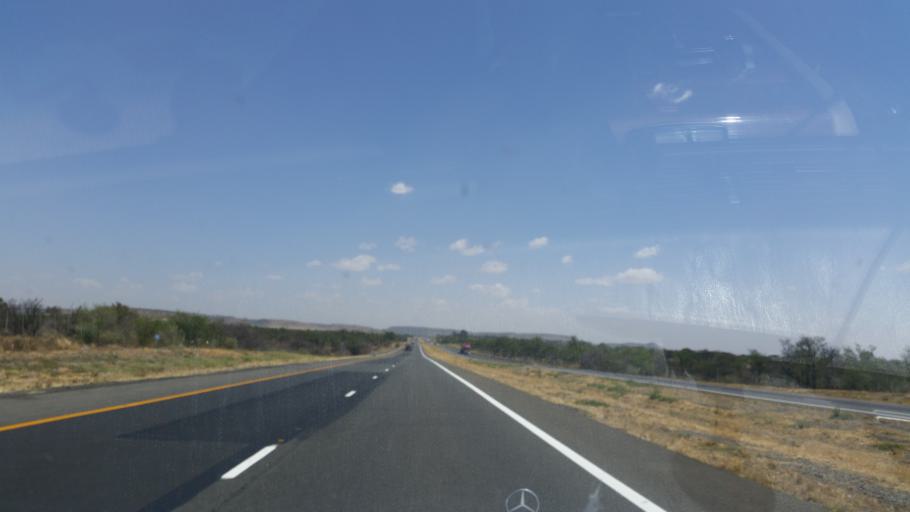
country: ZA
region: Orange Free State
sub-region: Mangaung Metropolitan Municipality
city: Bloemfontein
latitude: -28.9594
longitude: 26.3689
